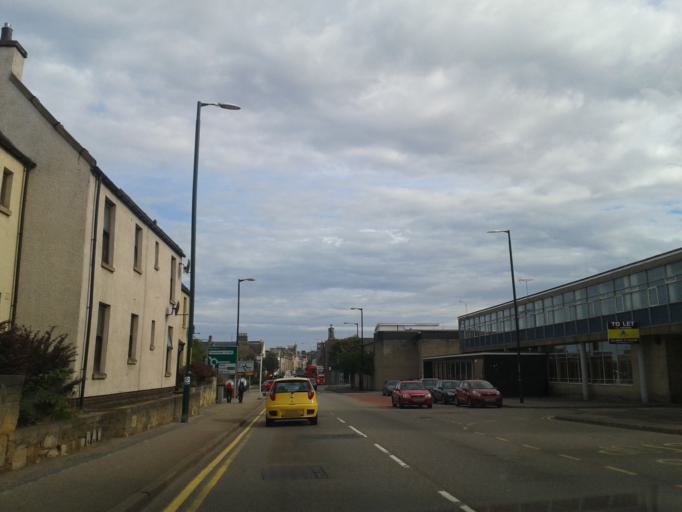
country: GB
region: Scotland
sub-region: Moray
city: Elgin
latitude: 57.6472
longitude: -3.3225
